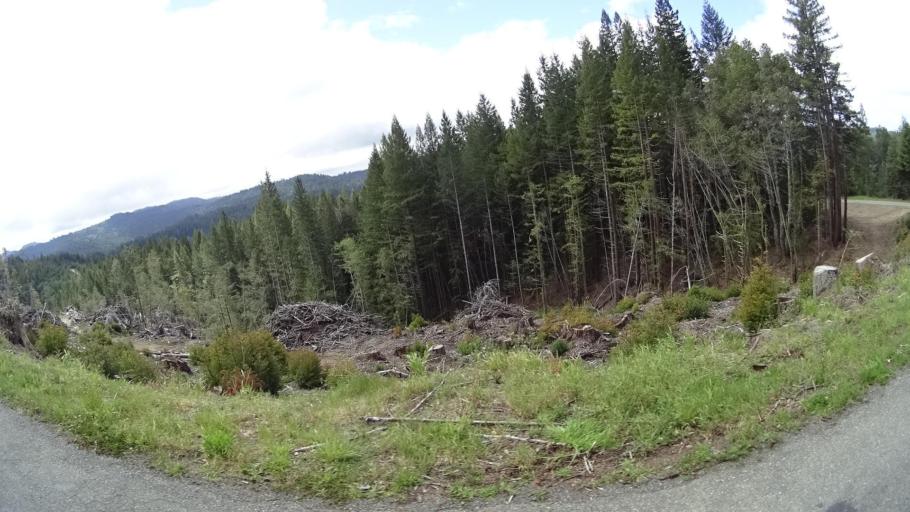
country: US
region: California
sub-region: Humboldt County
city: Blue Lake
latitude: 40.7774
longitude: -123.9641
